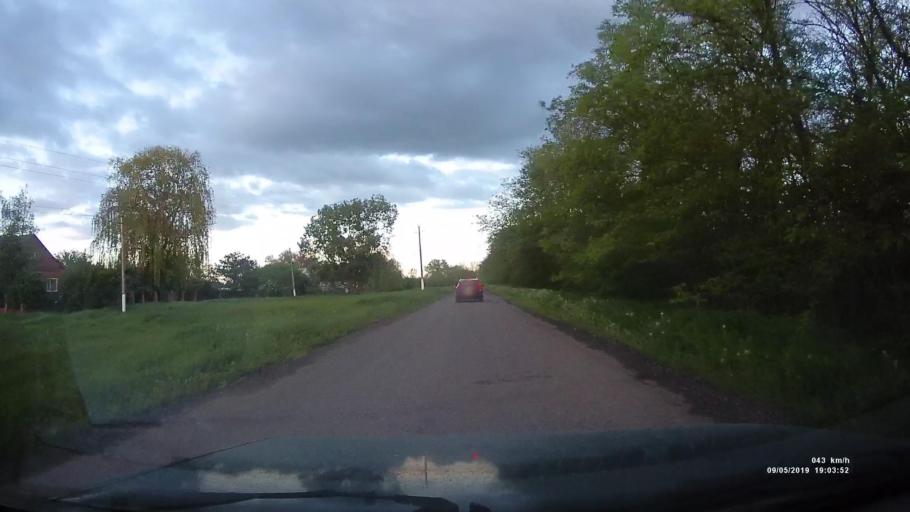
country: RU
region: Krasnodarskiy
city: Kanelovskaya
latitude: 46.7416
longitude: 39.1670
